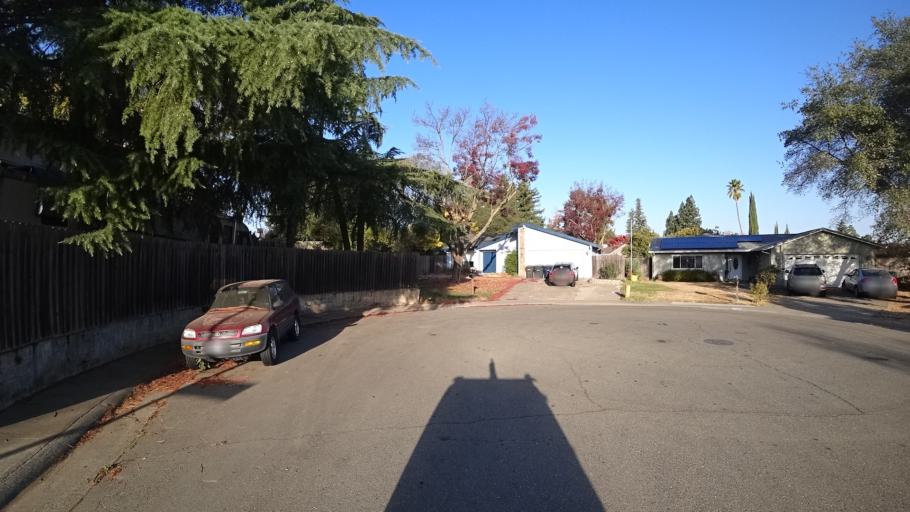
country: US
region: California
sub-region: Sacramento County
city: Citrus Heights
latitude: 38.7073
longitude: -121.2509
